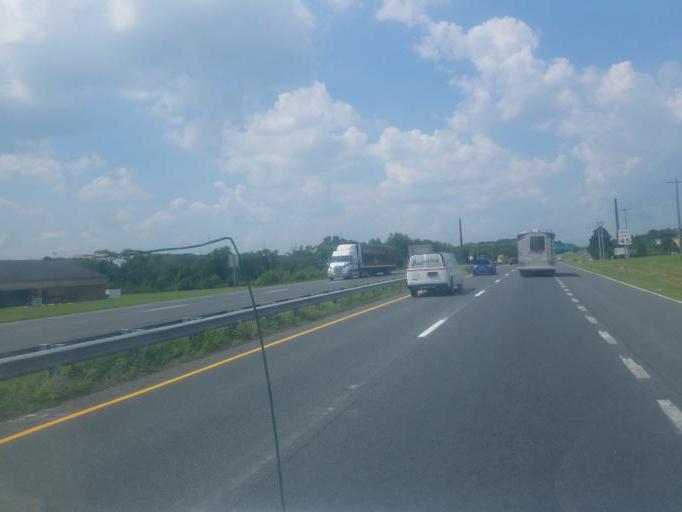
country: US
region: Maryland
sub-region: Worcester County
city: Berlin
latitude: 38.3360
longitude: -75.2113
